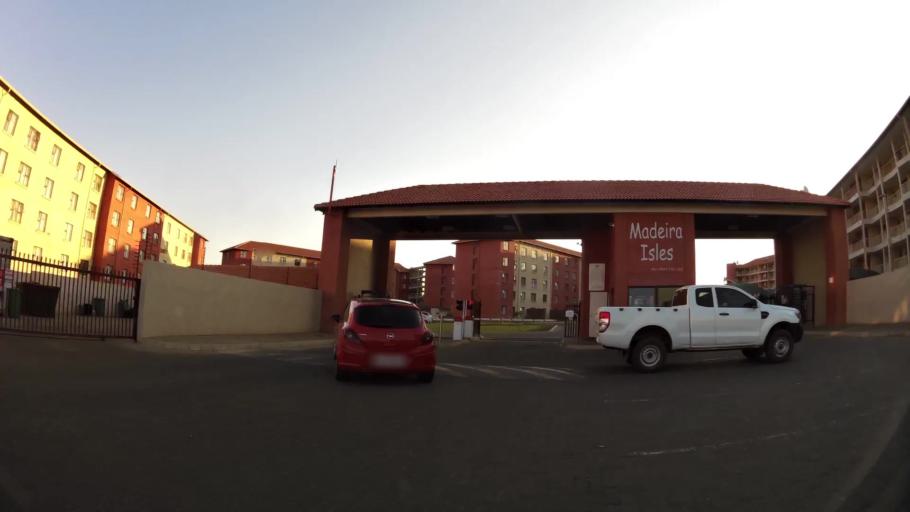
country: ZA
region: Gauteng
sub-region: City of Tshwane Metropolitan Municipality
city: Pretoria
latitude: -25.7479
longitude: 28.1133
